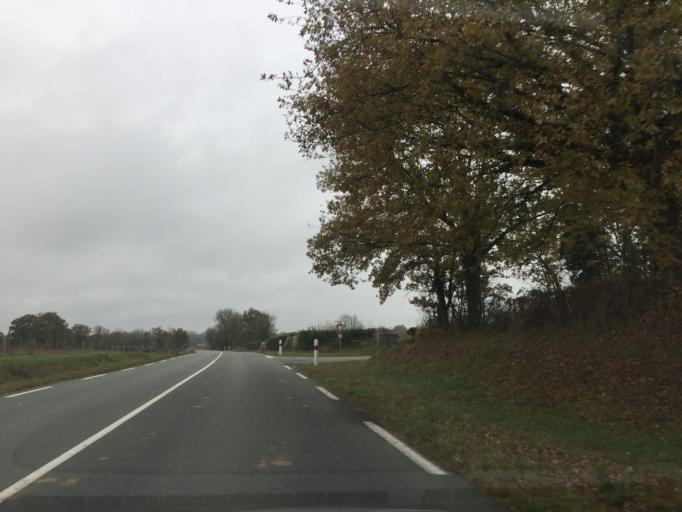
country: FR
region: Limousin
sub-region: Departement de la Creuse
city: Gouzon
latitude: 46.1302
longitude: 2.1903
